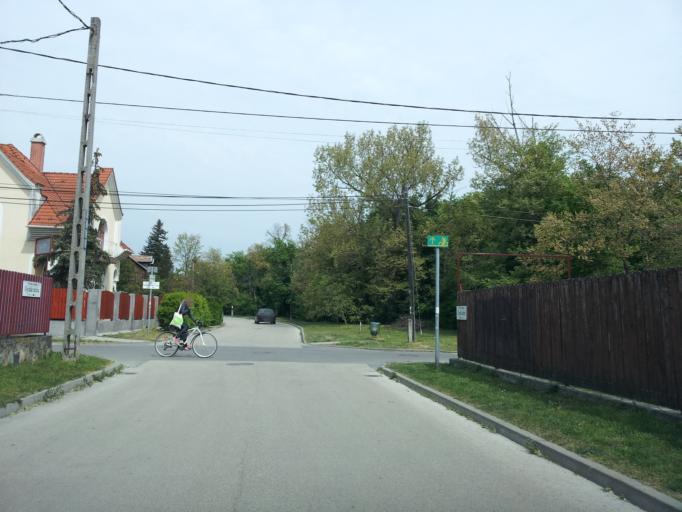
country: HU
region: Pest
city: Budakalasz
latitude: 47.5903
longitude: 19.0636
